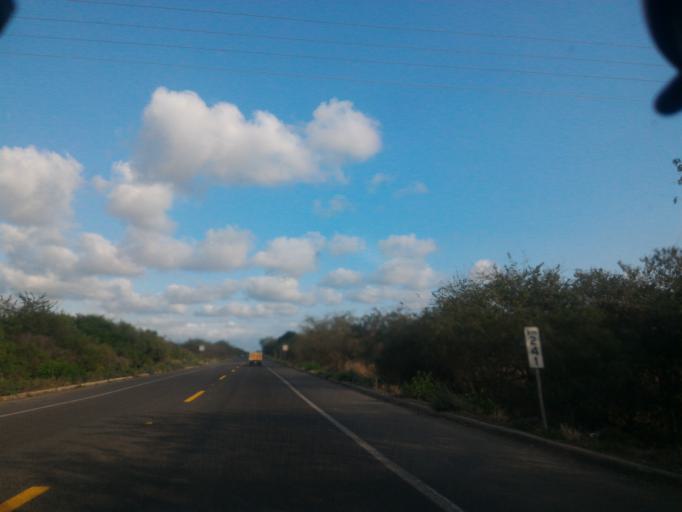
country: MX
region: Michoacan
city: Coahuayana Viejo
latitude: 18.7868
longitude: -103.7815
